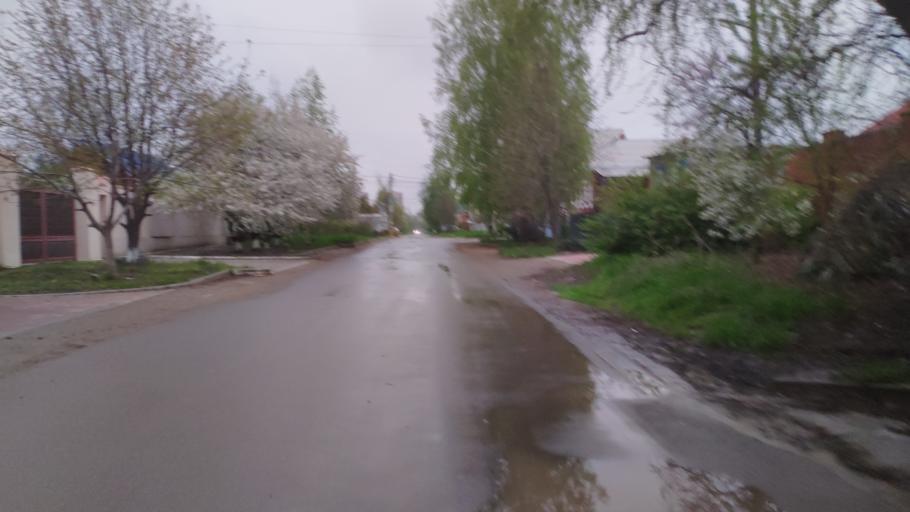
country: RU
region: Krasnodarskiy
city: Krasnodar
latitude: 45.0744
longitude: 39.0123
